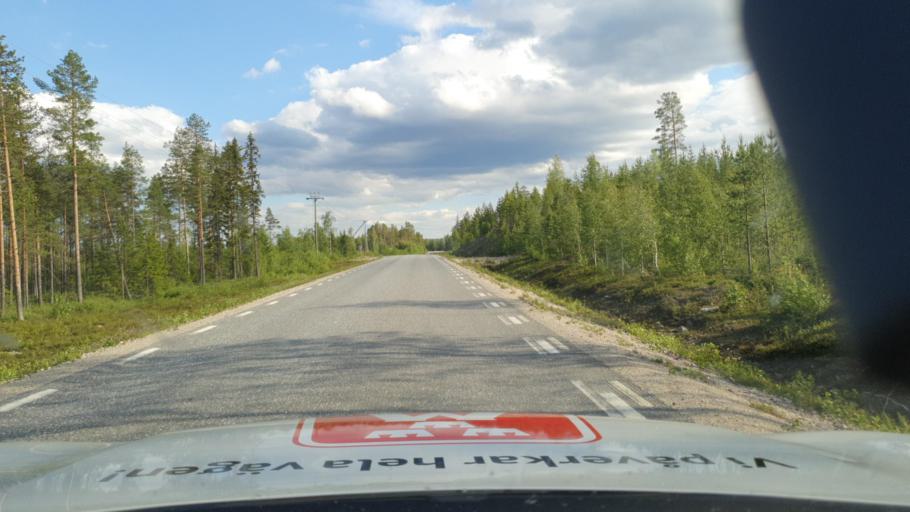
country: SE
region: Vaesterbotten
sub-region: Vindelns Kommun
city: Vindeln
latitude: 64.5080
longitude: 19.7951
